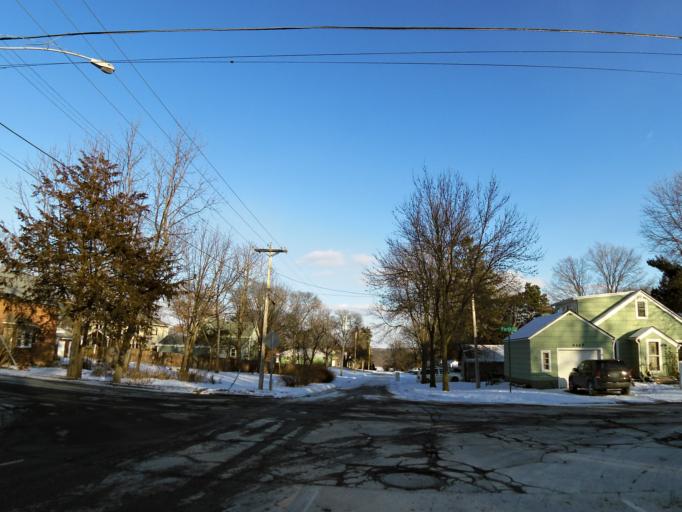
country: US
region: Minnesota
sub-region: Washington County
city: Oak Park Heights
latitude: 45.0428
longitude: -92.8001
